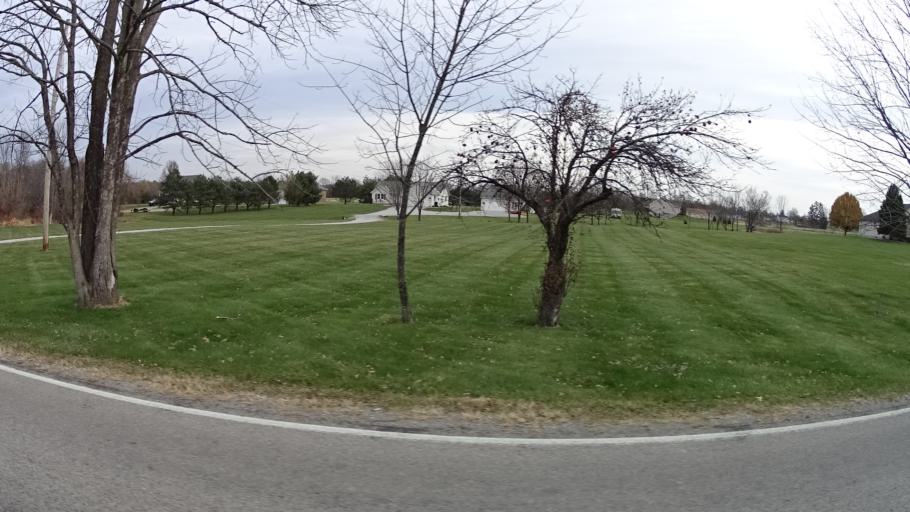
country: US
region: Ohio
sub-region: Lorain County
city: Lagrange
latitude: 41.1698
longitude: -82.0963
